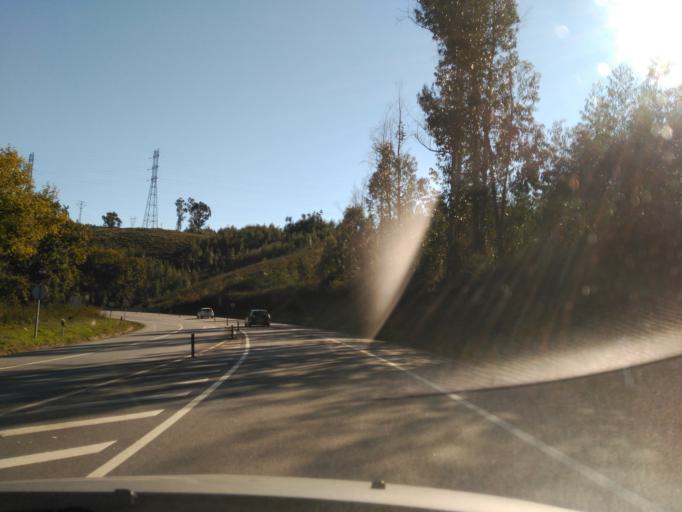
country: PT
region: Braga
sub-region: Povoa de Lanhoso
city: Povoa de Lanhoso
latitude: 41.5848
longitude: -8.3211
